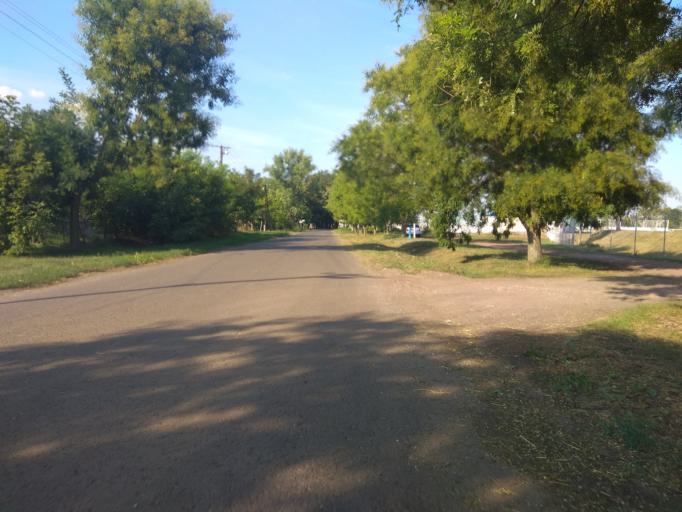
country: HU
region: Borsod-Abauj-Zemplen
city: Mezokeresztes
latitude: 47.8343
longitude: 20.6947
